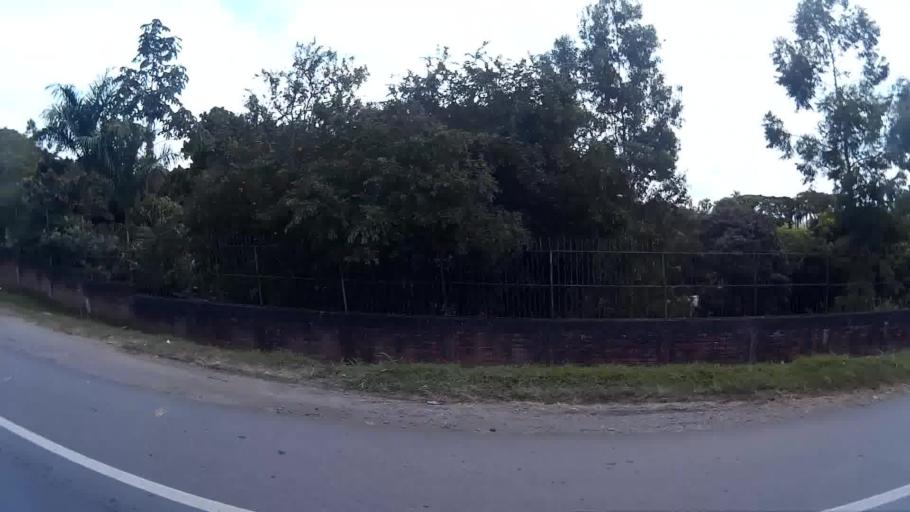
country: CO
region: Valle del Cauca
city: Cartago
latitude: 4.8026
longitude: -75.8382
